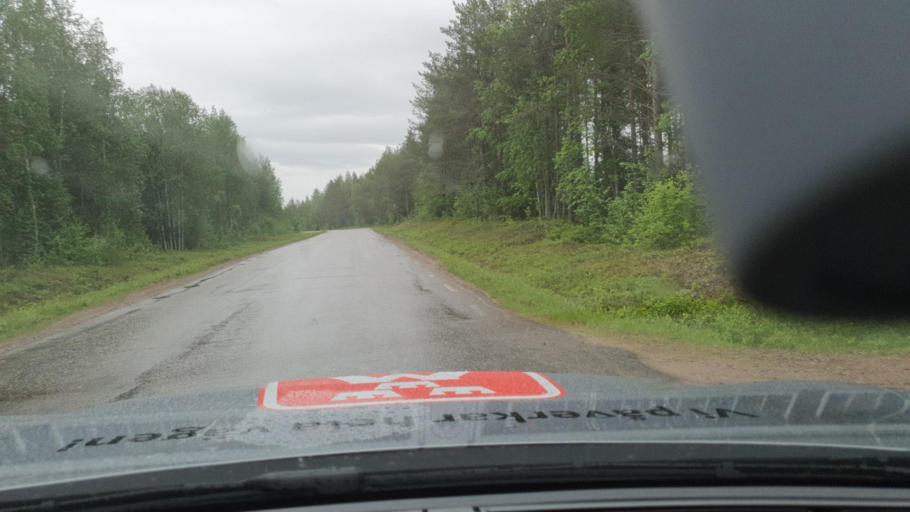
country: SE
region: Norrbotten
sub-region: Pajala Kommun
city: Pajala
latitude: 66.8436
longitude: 23.0724
